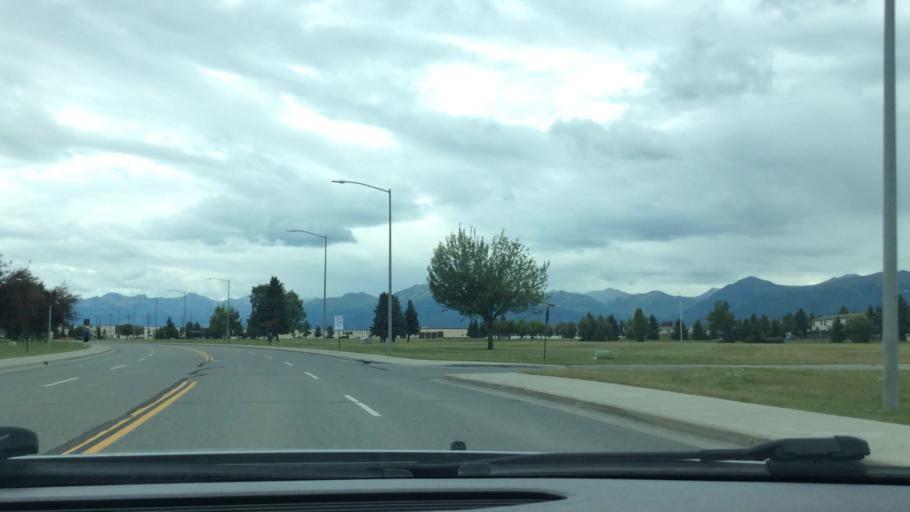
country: US
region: Alaska
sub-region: Anchorage Municipality
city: Anchorage
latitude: 61.2353
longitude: -149.8568
